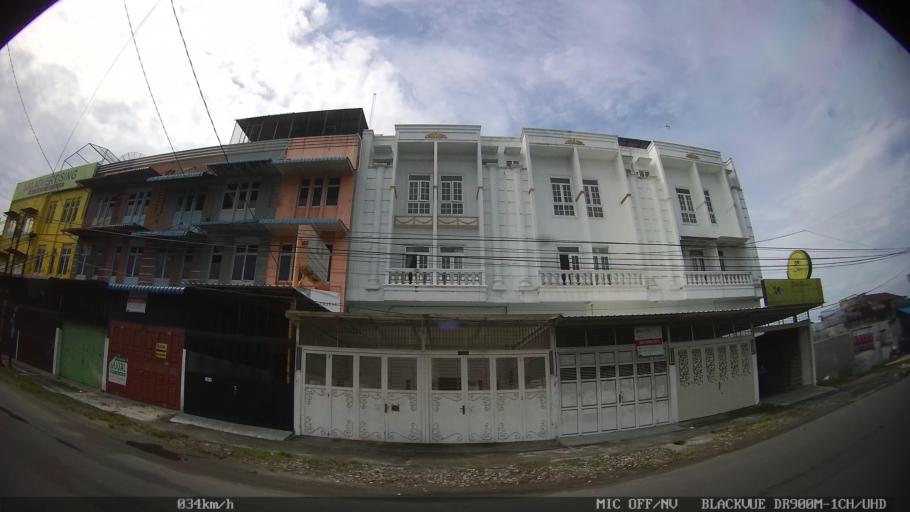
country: ID
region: North Sumatra
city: Medan
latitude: 3.6228
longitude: 98.6845
